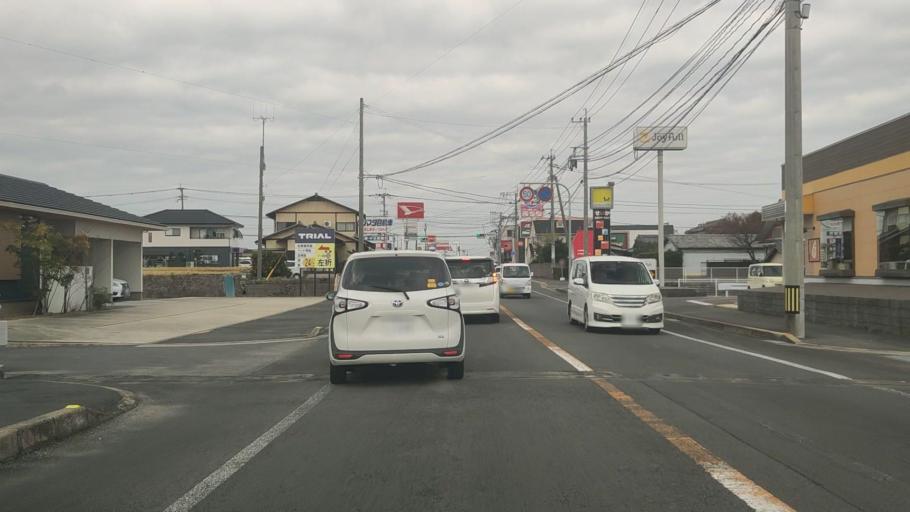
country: JP
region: Nagasaki
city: Shimabara
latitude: 32.8033
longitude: 130.3633
